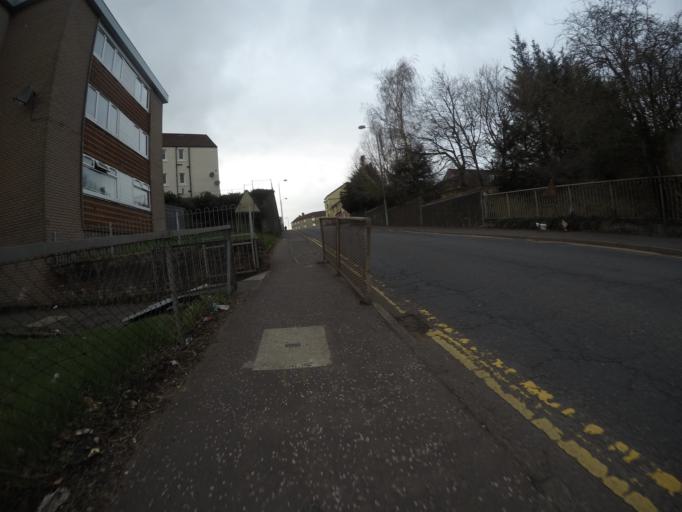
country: GB
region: Scotland
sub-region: East Ayrshire
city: Kilmarnock
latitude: 55.6148
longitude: -4.4935
